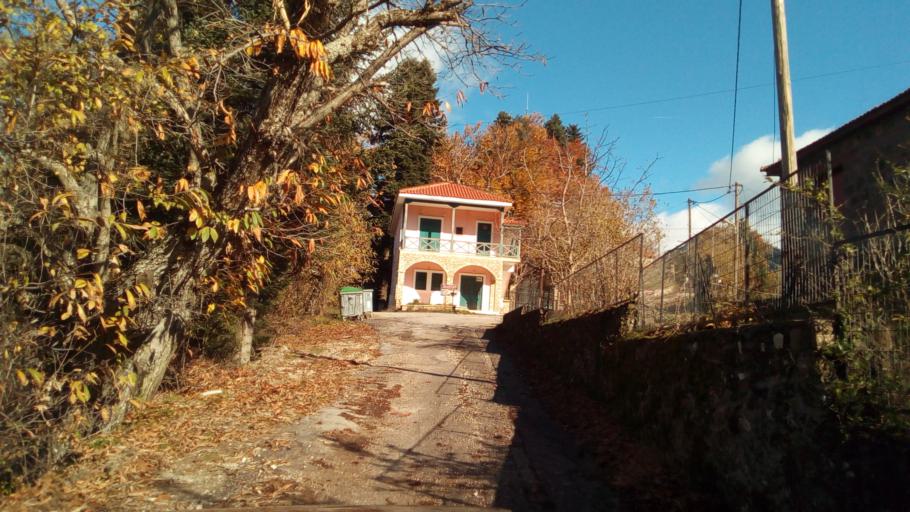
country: GR
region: West Greece
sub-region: Nomos Aitolias kai Akarnanias
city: Nafpaktos
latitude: 38.5935
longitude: 21.9236
